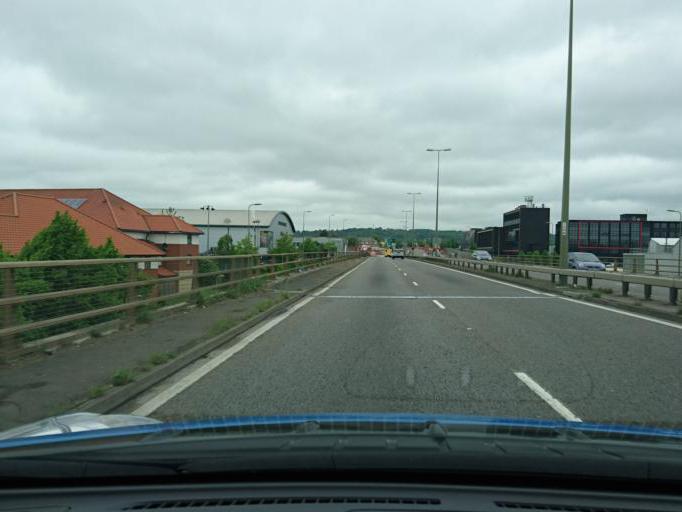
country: GB
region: England
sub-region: Oxfordshire
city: Cowley
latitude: 51.7302
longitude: -1.2024
